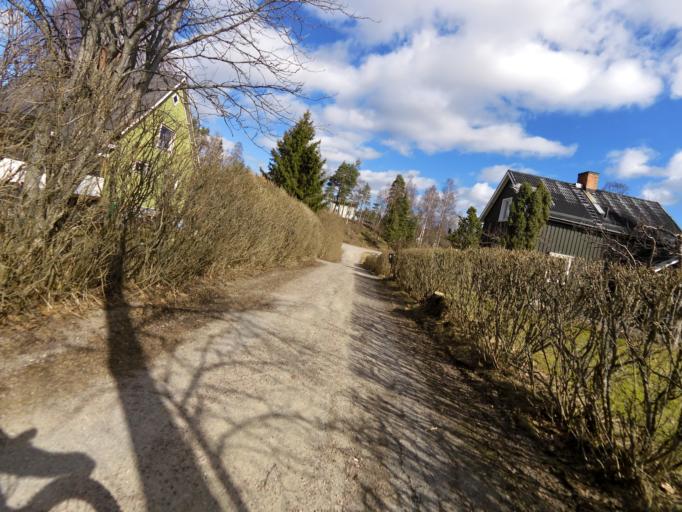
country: SE
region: Gaevleborg
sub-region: Hofors Kommun
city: Hofors
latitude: 60.5380
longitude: 16.2953
